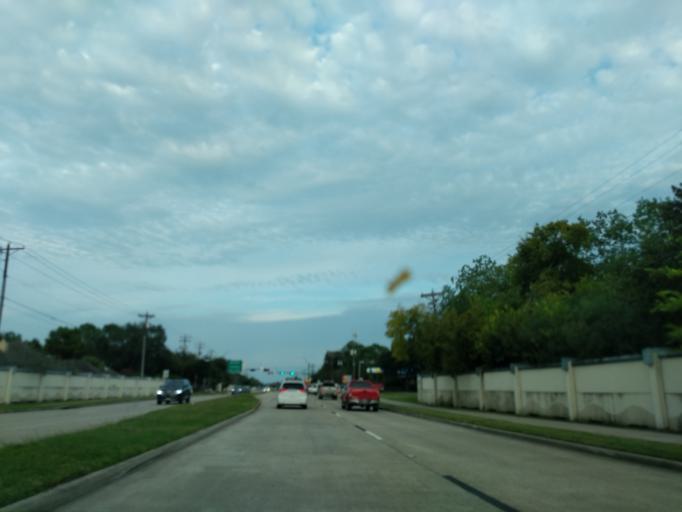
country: US
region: Texas
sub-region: Galveston County
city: Clear Lake Shores
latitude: 29.5251
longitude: -95.0563
